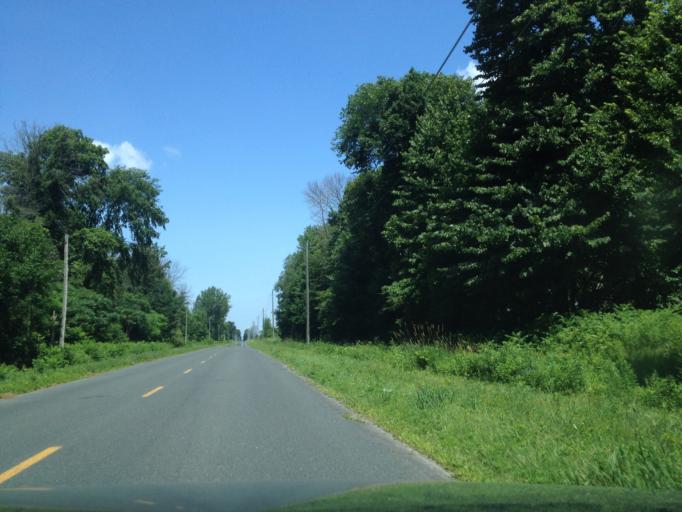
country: CA
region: Ontario
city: Aylmer
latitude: 42.6269
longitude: -80.7209
